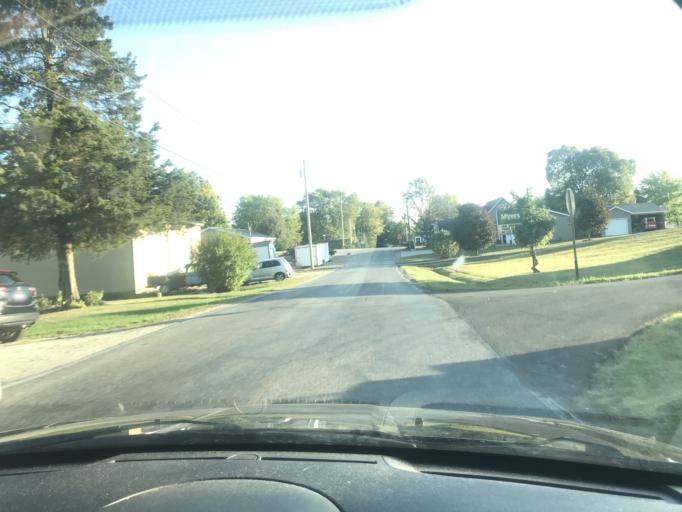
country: US
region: Ohio
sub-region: Logan County
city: De Graff
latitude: 40.2564
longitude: -83.8684
